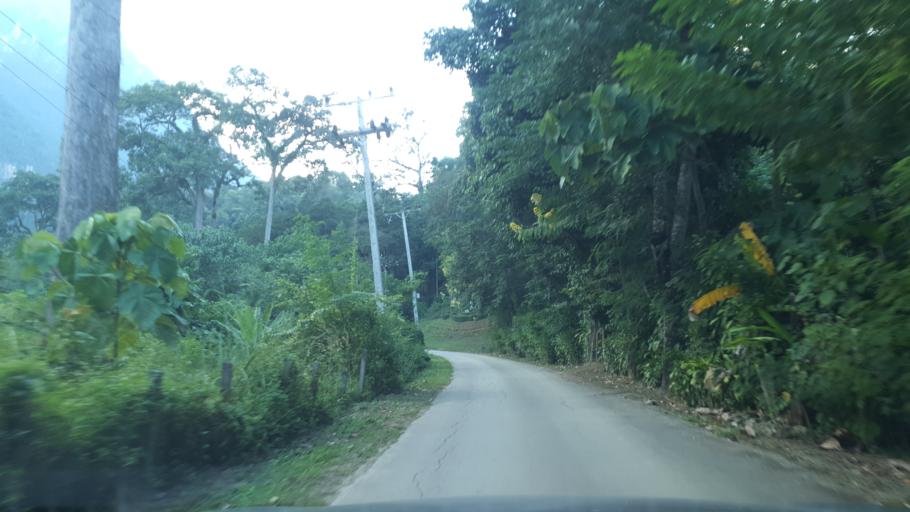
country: TH
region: Chiang Mai
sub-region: Amphoe Chiang Dao
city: Chiang Dao
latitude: 19.4040
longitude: 98.9246
